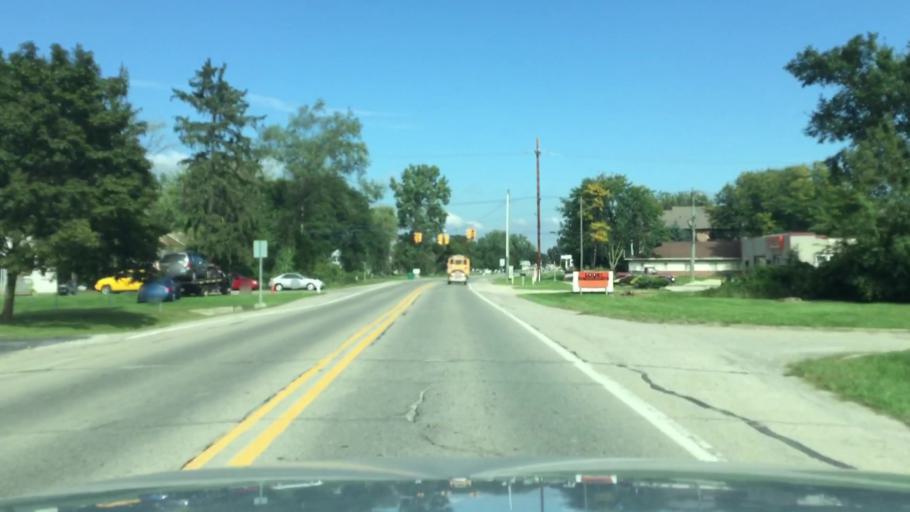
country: US
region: Michigan
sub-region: Wayne County
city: Belleville
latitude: 42.1963
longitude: -83.4847
